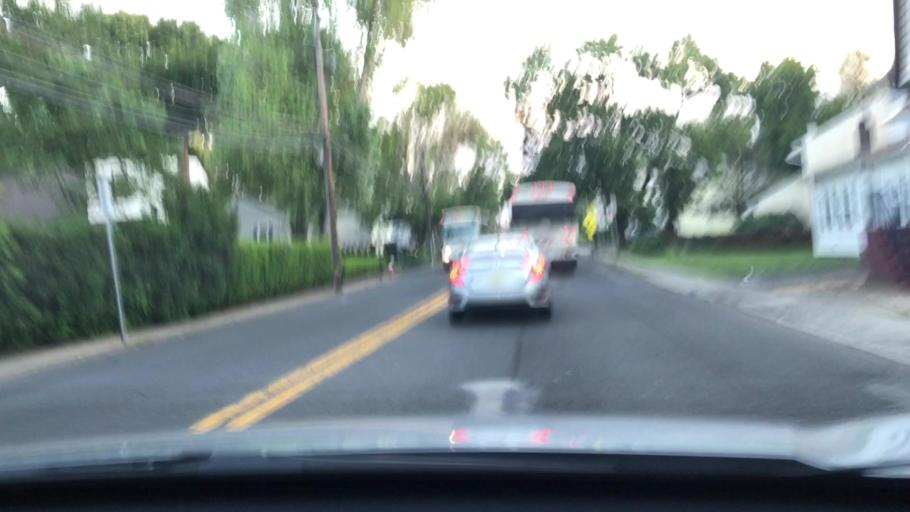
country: US
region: New Jersey
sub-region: Bergen County
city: Teaneck
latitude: 40.9069
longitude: -73.9988
